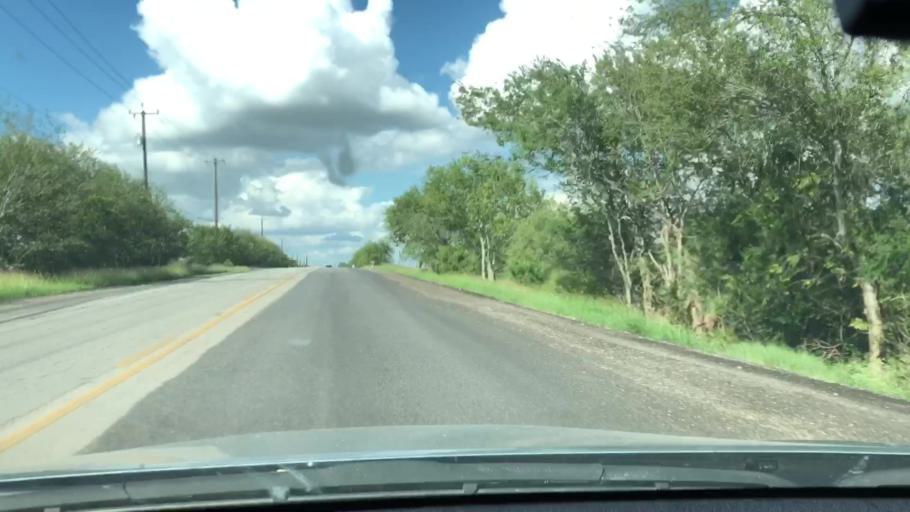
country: US
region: Texas
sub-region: Bexar County
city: Converse
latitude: 29.4824
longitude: -98.3125
